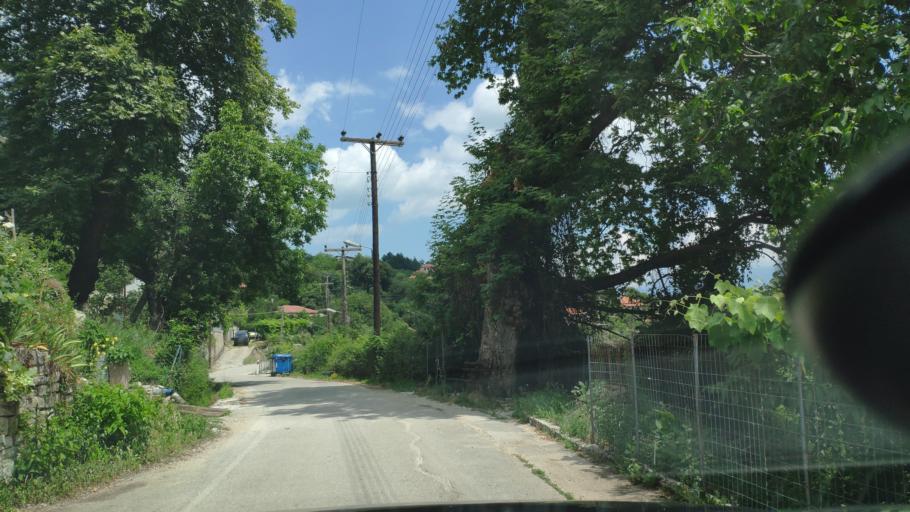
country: GR
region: Epirus
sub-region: Nomos Artas
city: Agios Dimitrios
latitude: 39.3238
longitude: 20.9972
